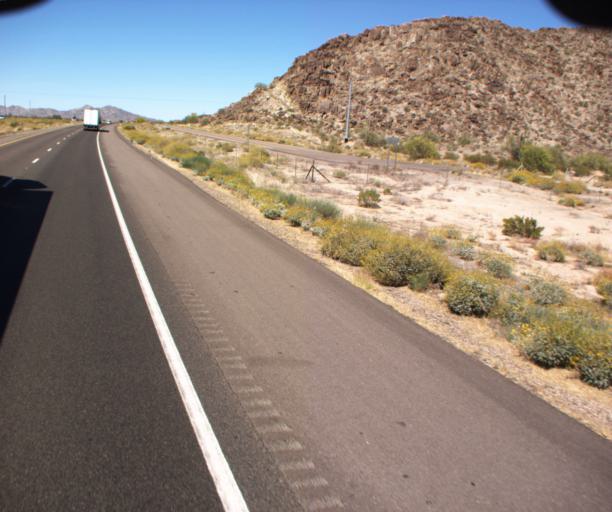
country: US
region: Arizona
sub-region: Maricopa County
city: Buckeye
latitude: 33.1702
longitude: -112.6502
